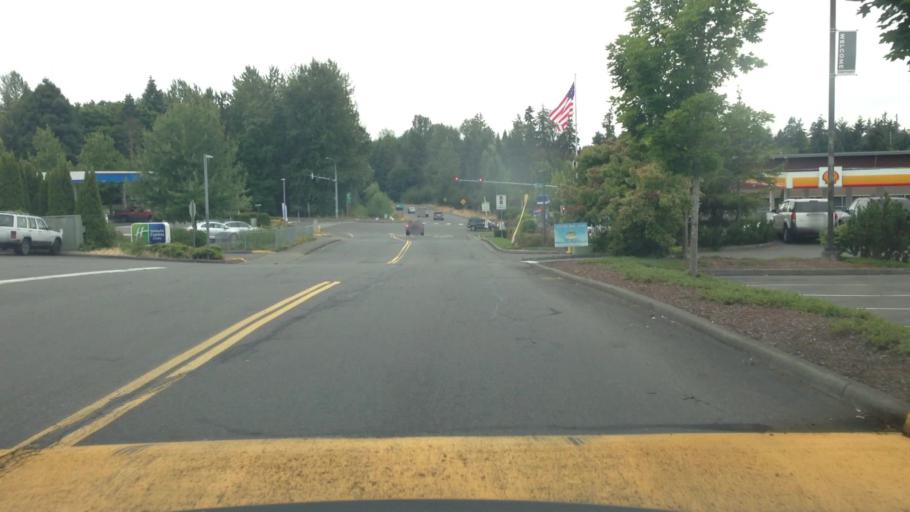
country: US
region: Washington
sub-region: Pierce County
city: Puyallup
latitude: 47.1609
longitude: -122.3024
